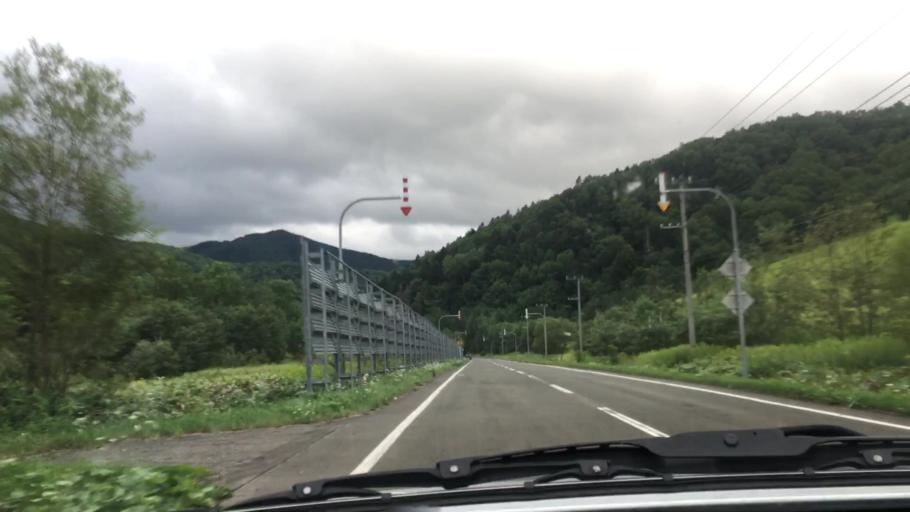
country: JP
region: Hokkaido
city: Shimo-furano
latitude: 43.0581
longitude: 142.5306
